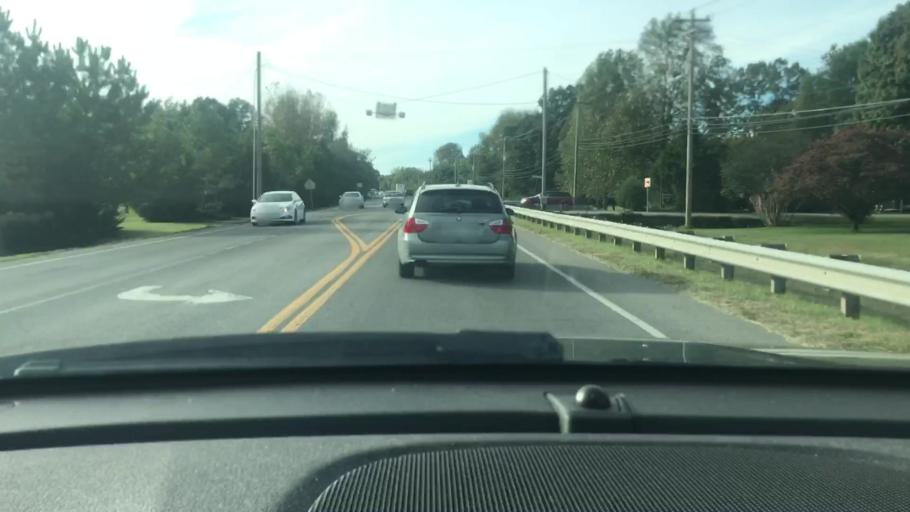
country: US
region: Tennessee
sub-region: Williamson County
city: Franklin
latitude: 35.9269
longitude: -86.8862
